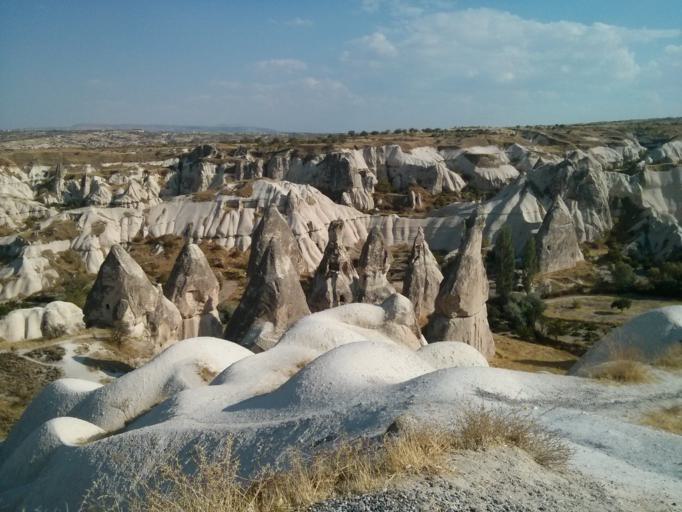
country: TR
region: Nevsehir
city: Goereme
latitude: 38.6405
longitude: 34.8178
